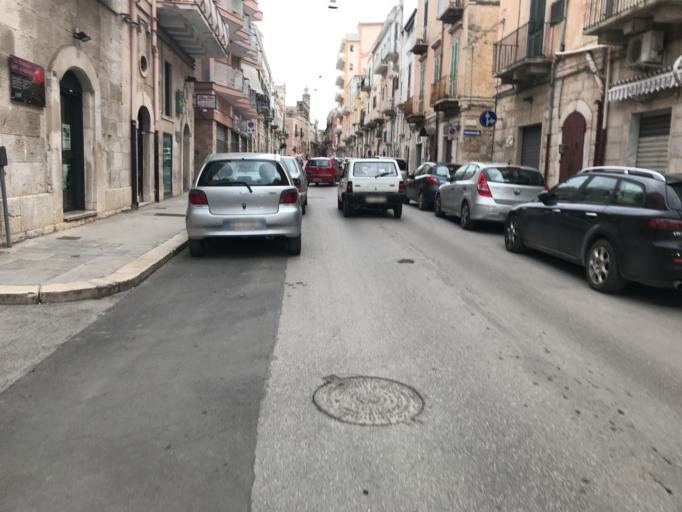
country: IT
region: Apulia
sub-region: Provincia di Bari
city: Corato
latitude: 41.1557
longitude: 16.4117
